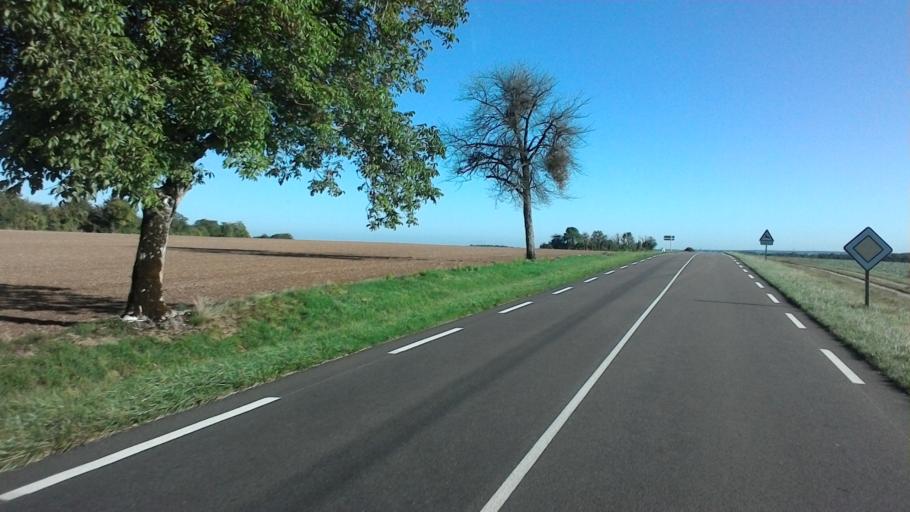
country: FR
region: Bourgogne
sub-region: Departement de la Cote-d'Or
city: Montbard
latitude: 47.7107
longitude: 4.4425
